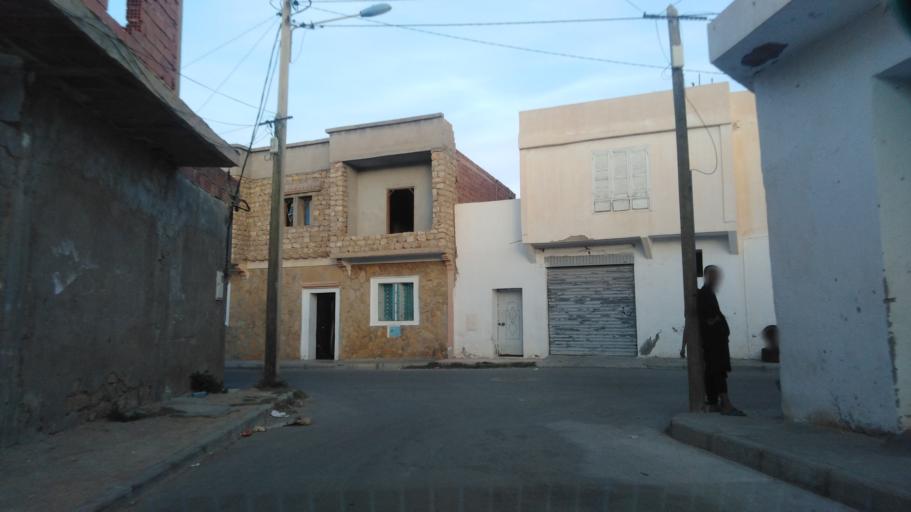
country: TN
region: Tataouine
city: Tataouine
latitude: 32.9371
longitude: 10.4556
